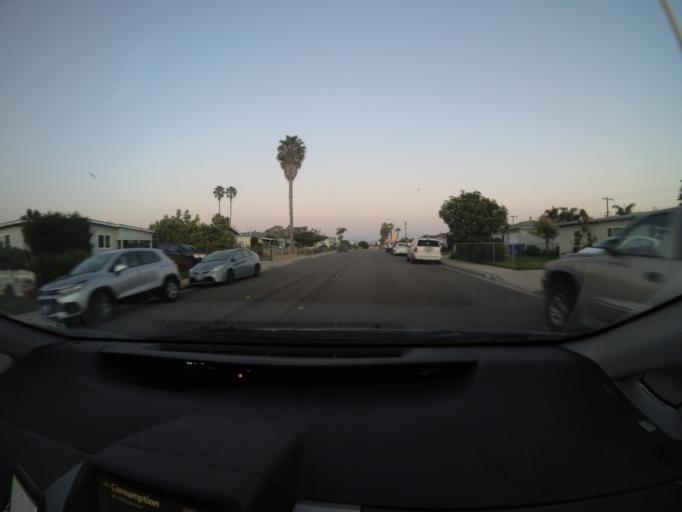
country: US
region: California
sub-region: San Diego County
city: Imperial Beach
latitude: 32.5803
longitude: -117.1264
